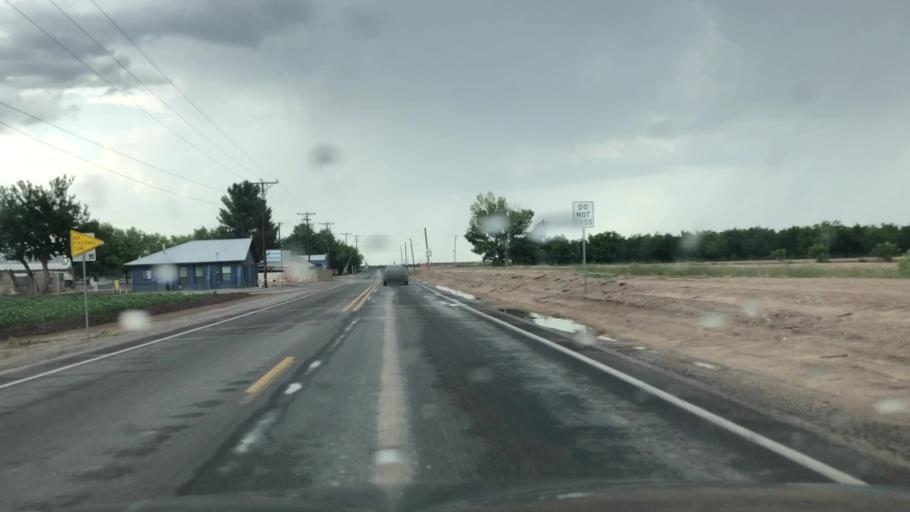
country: US
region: New Mexico
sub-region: Dona Ana County
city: Vado
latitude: 32.0591
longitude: -106.6766
